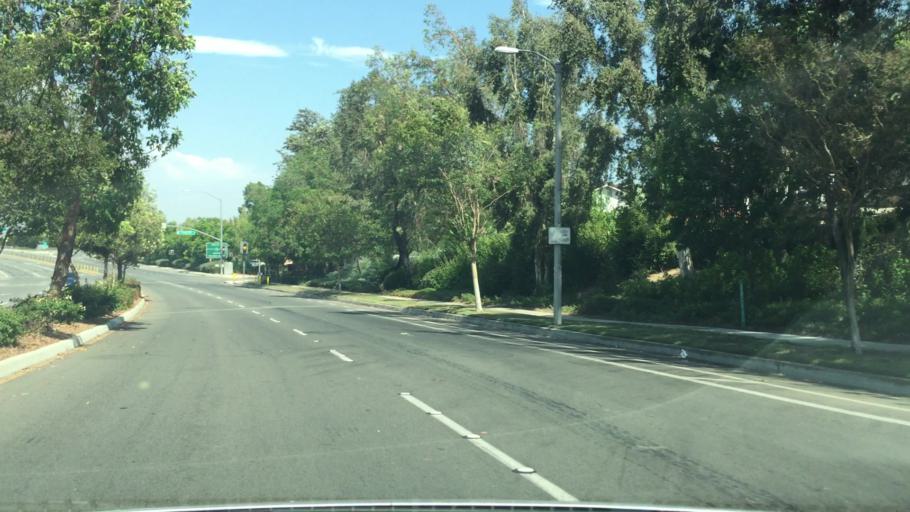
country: US
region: California
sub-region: San Bernardino County
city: Los Serranos
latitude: 33.9300
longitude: -117.6631
